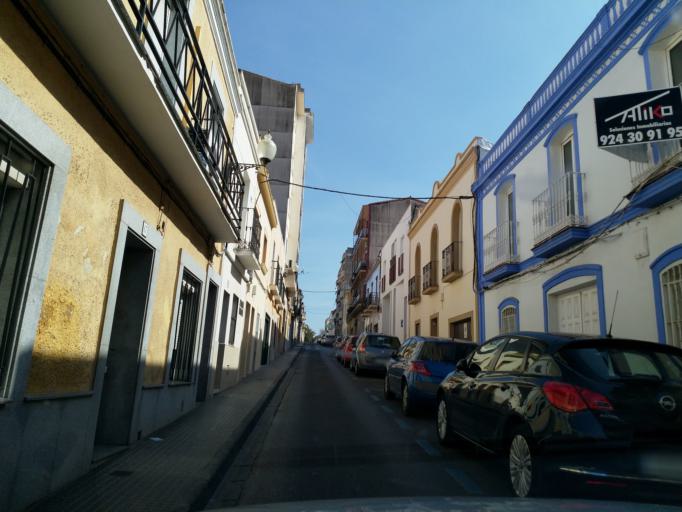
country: ES
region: Extremadura
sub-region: Provincia de Badajoz
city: Merida
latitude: 38.9156
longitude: -6.3415
